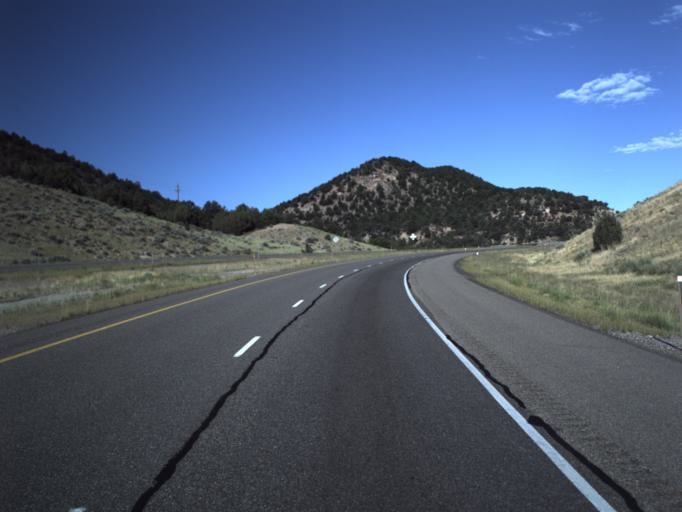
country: US
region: Utah
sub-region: Sevier County
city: Monroe
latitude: 38.5472
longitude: -112.3755
